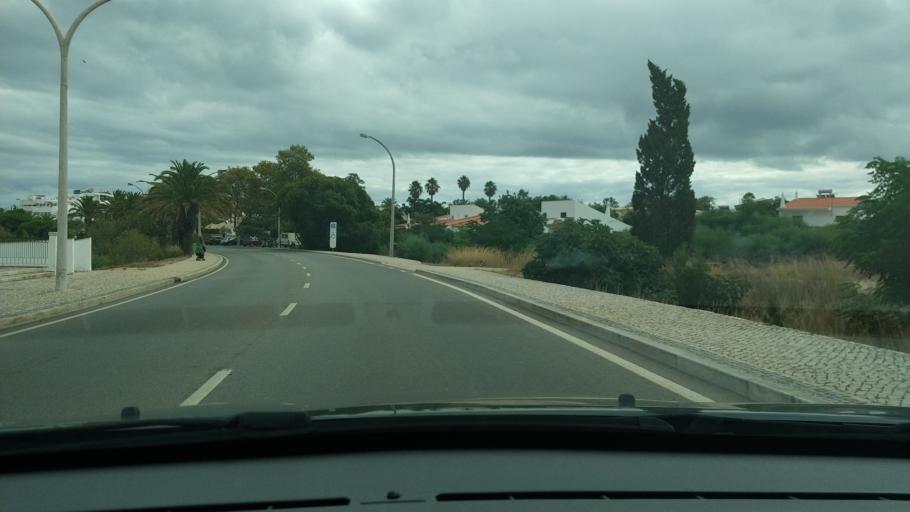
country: PT
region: Faro
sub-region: Lagos
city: Lagos
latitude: 37.0960
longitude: -8.6775
